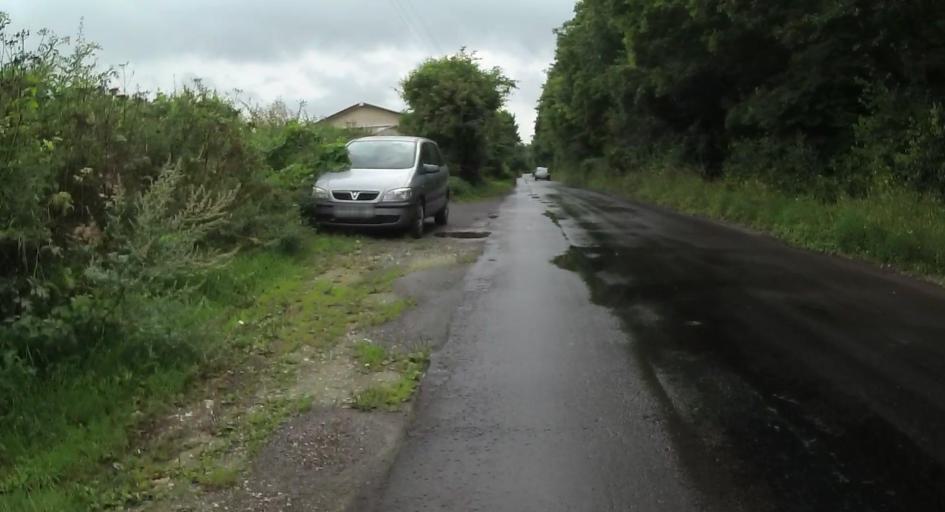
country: GB
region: England
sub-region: Hampshire
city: Andover
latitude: 51.2129
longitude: -1.4487
